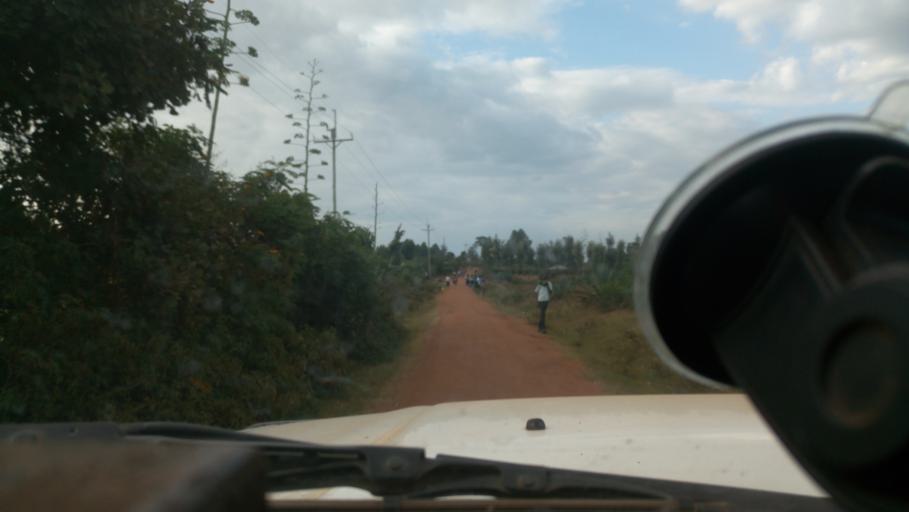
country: KE
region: Migori
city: Kihancha
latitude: -1.3383
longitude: 34.7068
